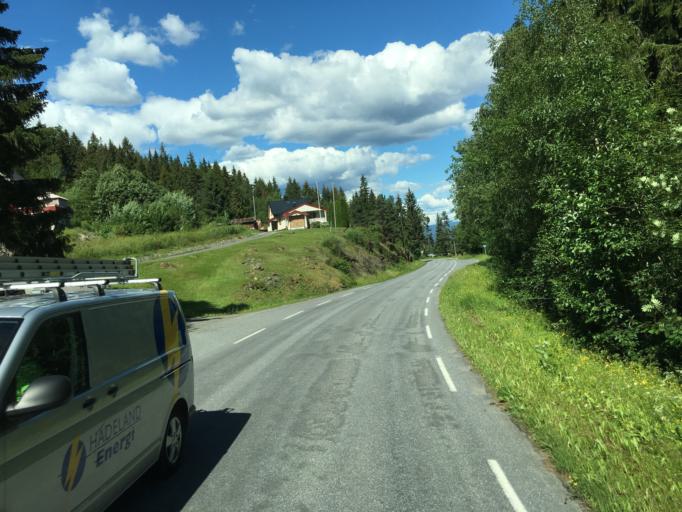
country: NO
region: Oppland
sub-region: Jevnaker
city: Jevnaker
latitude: 60.3130
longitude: 10.3425
